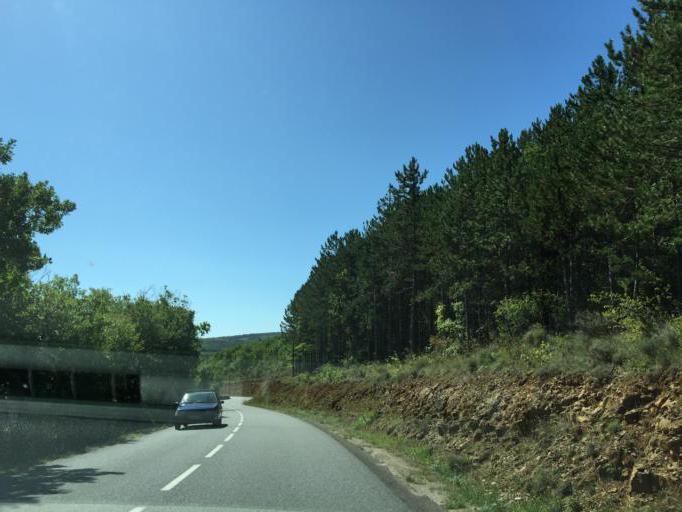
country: FR
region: Midi-Pyrenees
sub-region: Departement de l'Aveyron
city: Saint-Georges-de-Luzencon
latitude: 44.0694
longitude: 2.9052
